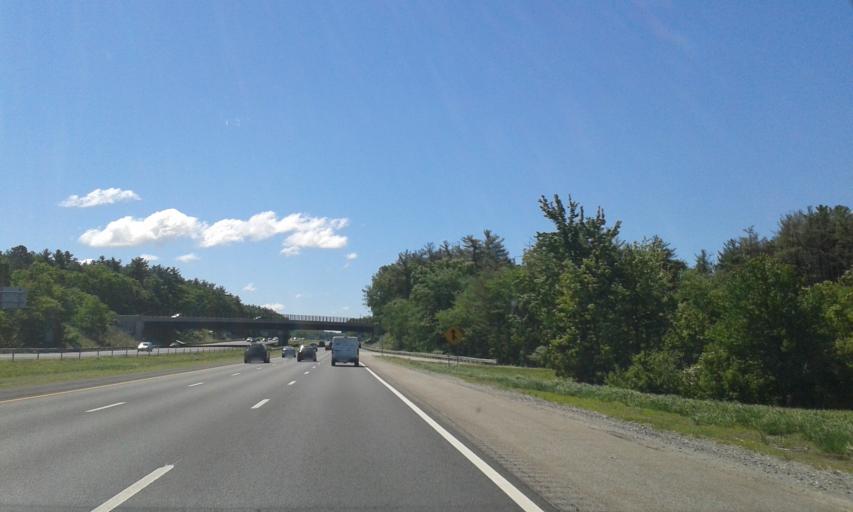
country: US
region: Massachusetts
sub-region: Middlesex County
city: Billerica
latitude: 42.5623
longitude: -71.2993
